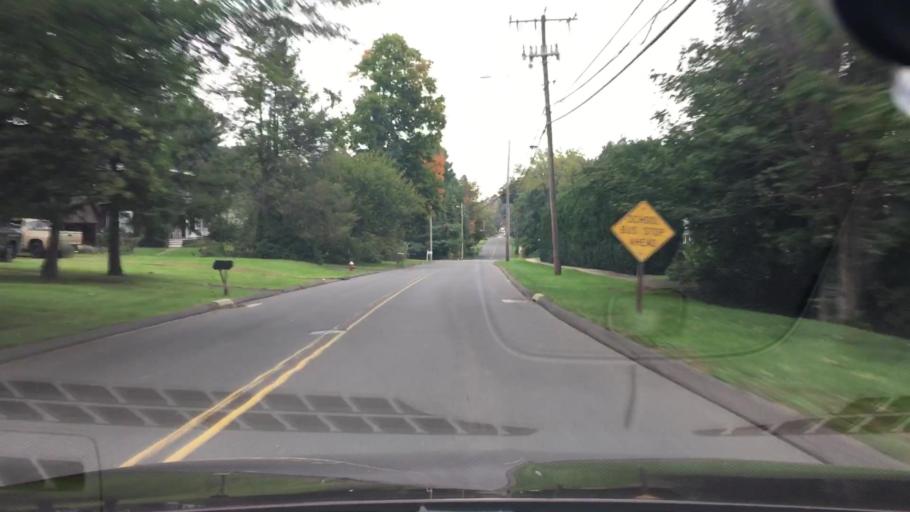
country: US
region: Connecticut
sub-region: Hartford County
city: Kensington
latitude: 41.6045
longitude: -72.7199
